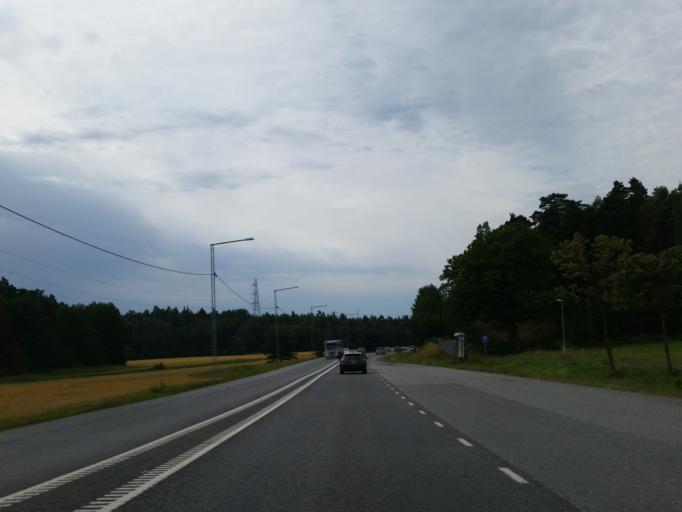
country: SE
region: Stockholm
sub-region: Botkyrka Kommun
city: Alby
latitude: 59.2272
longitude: 17.8397
